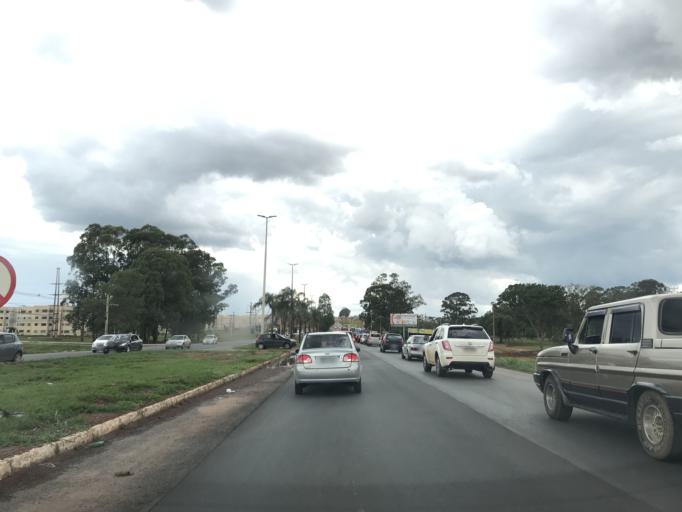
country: BR
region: Federal District
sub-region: Brasilia
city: Brasilia
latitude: -15.8889
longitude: -48.0583
